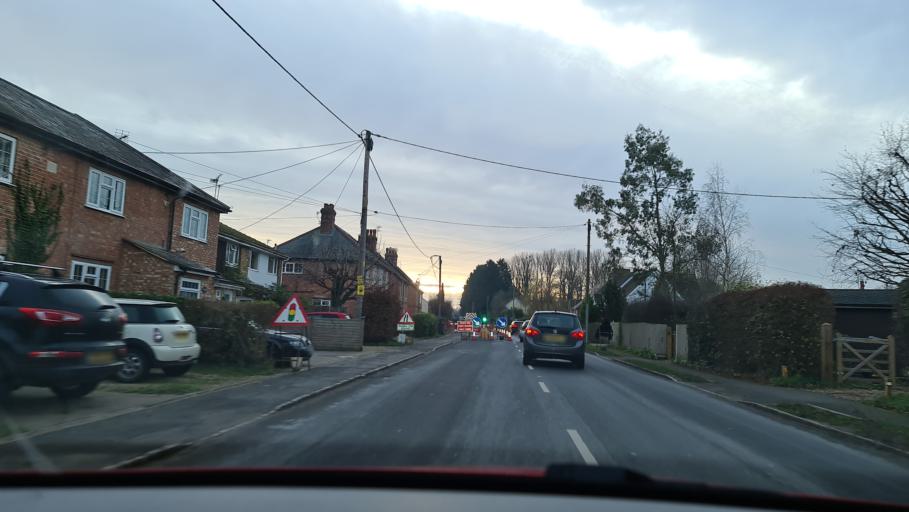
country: GB
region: England
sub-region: Buckinghamshire
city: Princes Risborough
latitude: 51.7426
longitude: -0.8654
